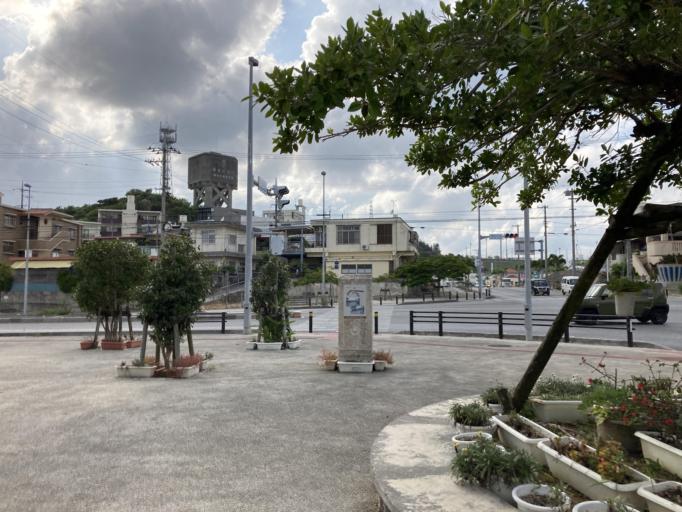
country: JP
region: Okinawa
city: Tomigusuku
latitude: 26.1550
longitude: 127.7214
